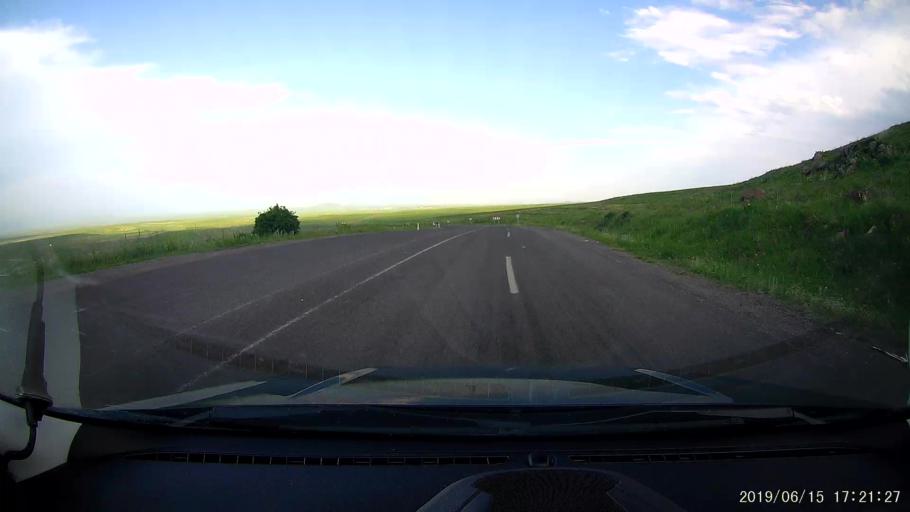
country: TR
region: Kars
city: Basgedikler
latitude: 40.6173
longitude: 43.3250
